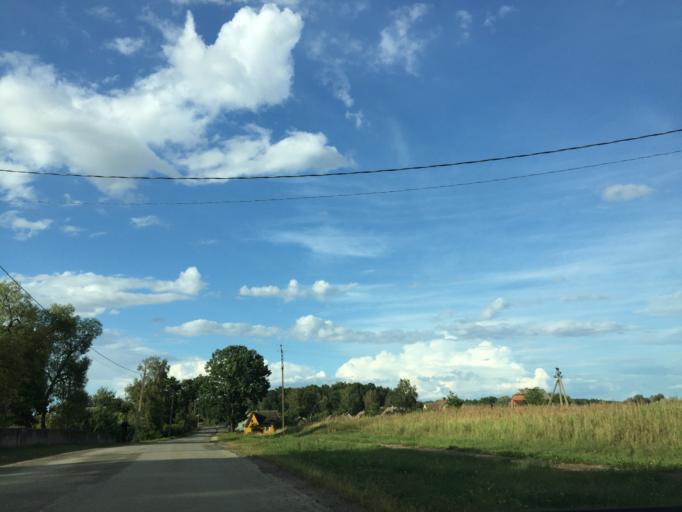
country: LT
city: Zagare
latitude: 56.3659
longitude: 23.2639
